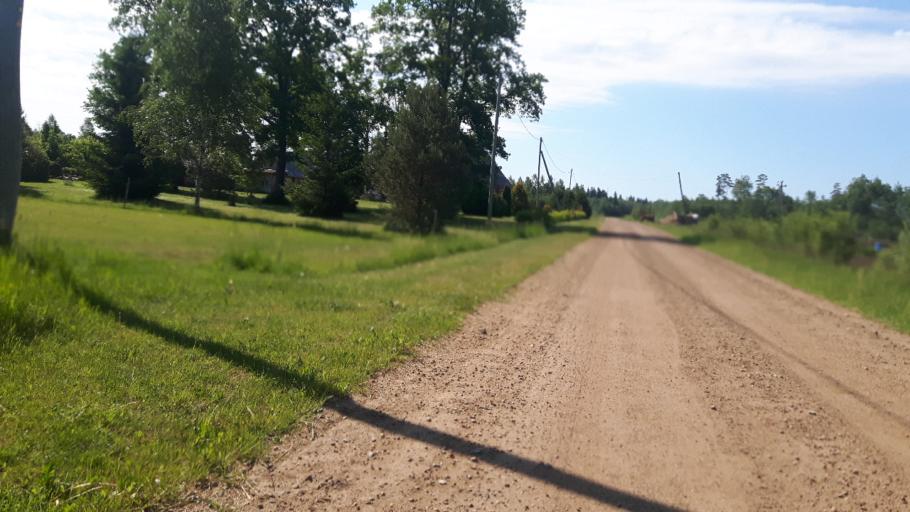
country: EE
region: Paernumaa
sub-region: Vaendra vald (alev)
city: Vandra
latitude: 58.6735
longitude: 25.0298
